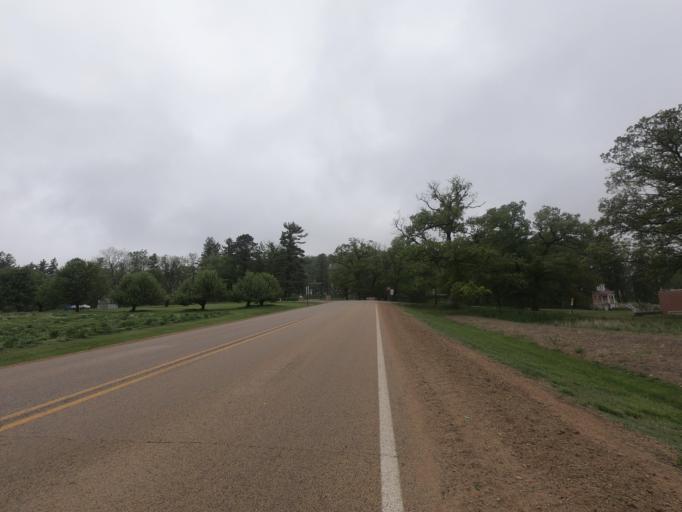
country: US
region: Illinois
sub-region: Jo Daviess County
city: East Dubuque
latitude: 42.5213
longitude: -90.5441
